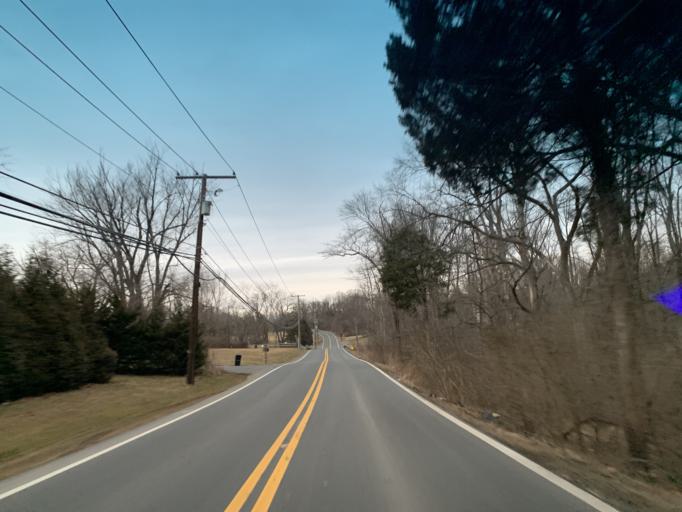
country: US
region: Maryland
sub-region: Montgomery County
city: Layhill
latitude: 39.1052
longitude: -77.0386
